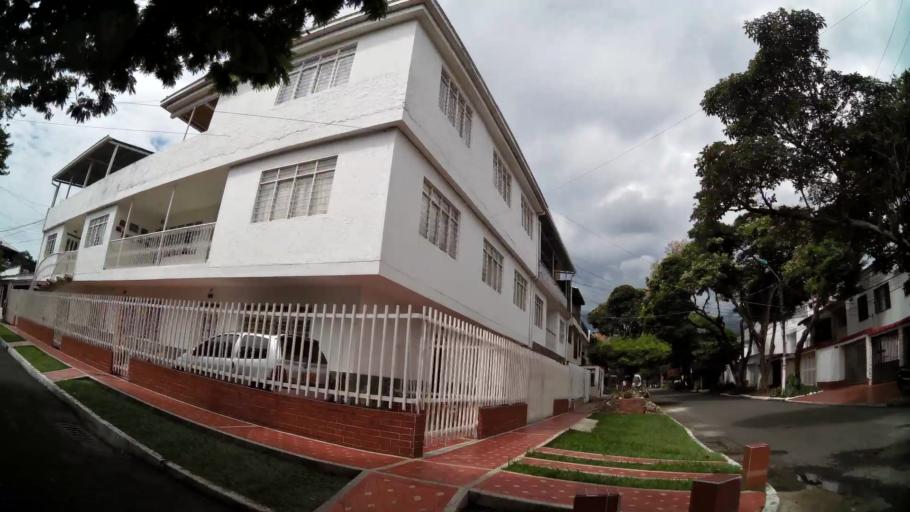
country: CO
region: Valle del Cauca
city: Cali
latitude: 3.3957
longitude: -76.5503
